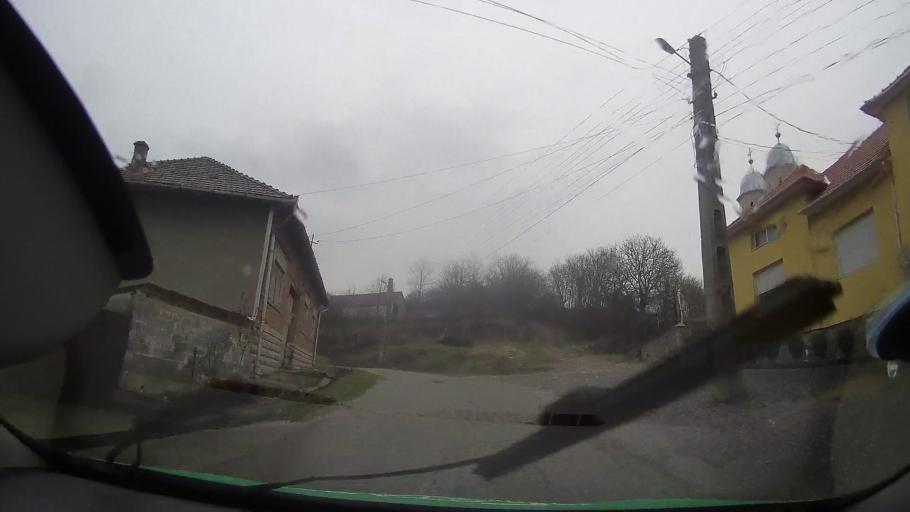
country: RO
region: Bihor
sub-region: Comuna Uileacu de Beius
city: Uileacu de Beius
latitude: 46.7114
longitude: 22.2281
